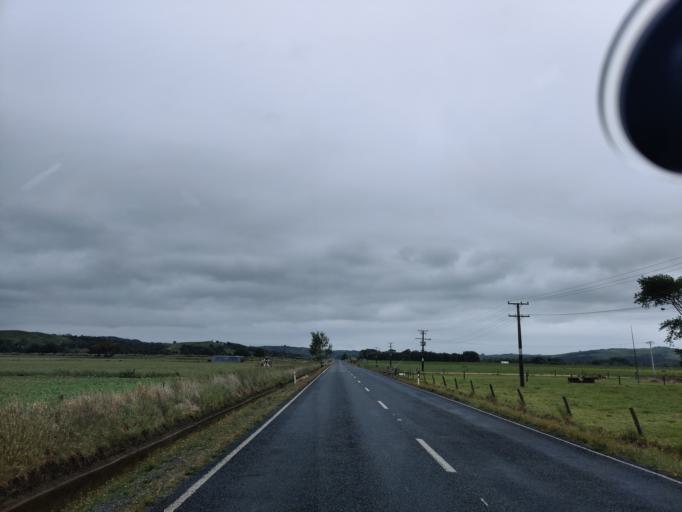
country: NZ
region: Northland
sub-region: Kaipara District
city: Dargaville
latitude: -36.1191
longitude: 174.0707
